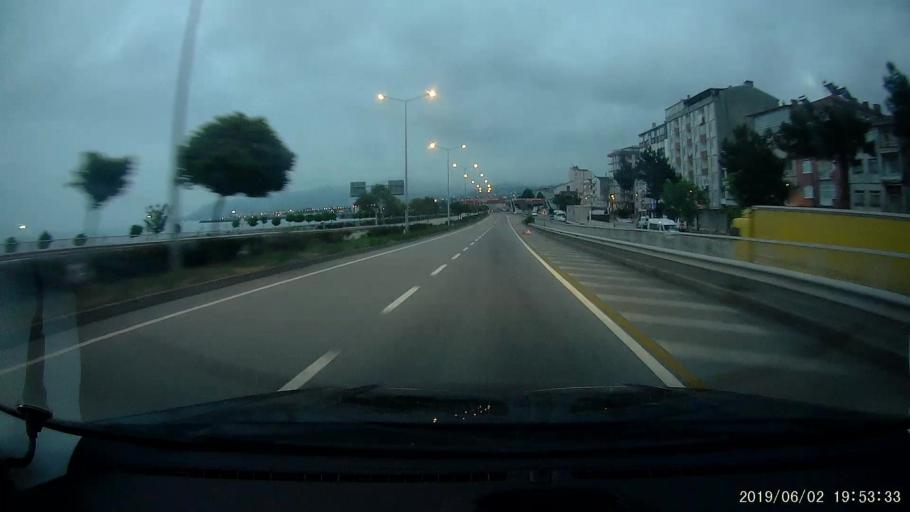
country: TR
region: Trabzon
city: Espiye
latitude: 40.9500
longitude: 38.7088
